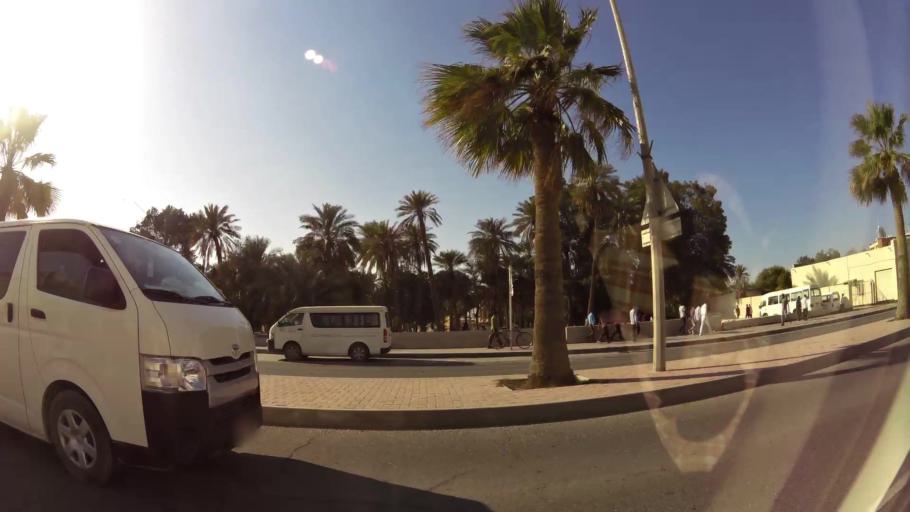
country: BH
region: Manama
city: Manama
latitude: 26.2221
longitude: 50.5697
